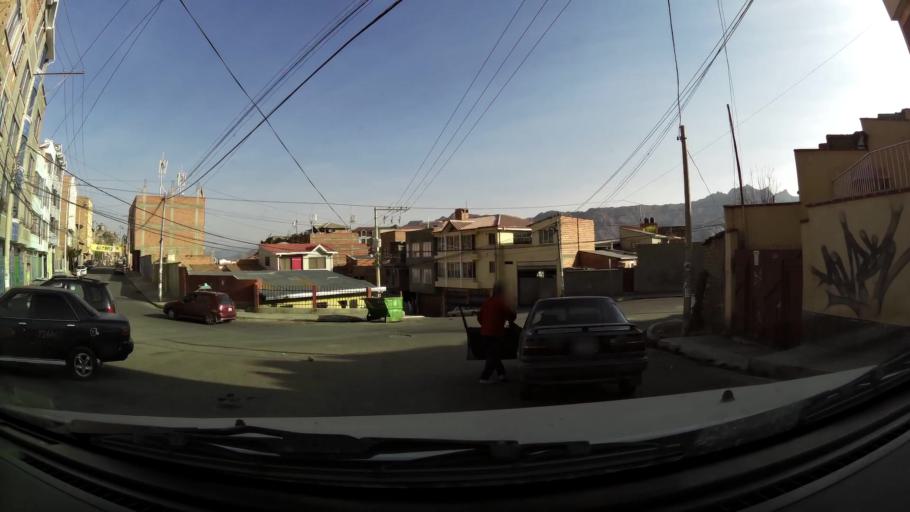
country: BO
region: La Paz
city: La Paz
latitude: -16.5271
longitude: -68.0954
